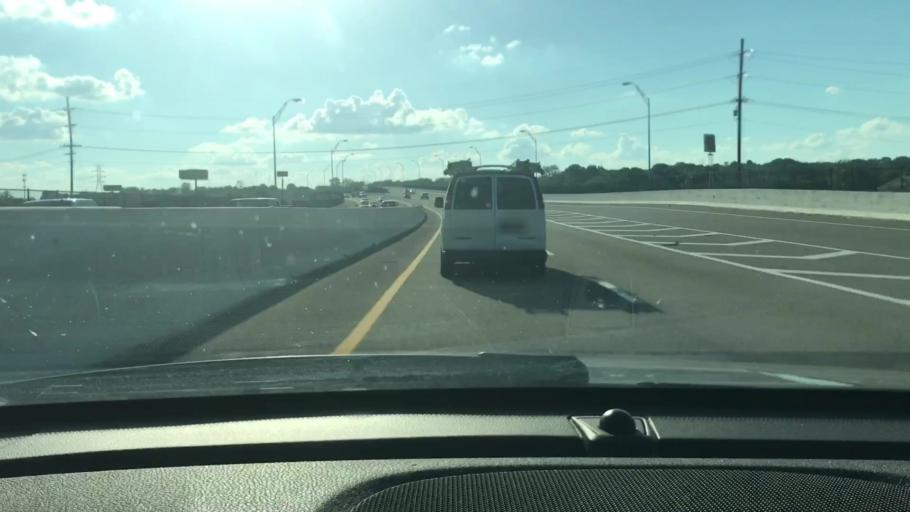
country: US
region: Tennessee
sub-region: Davidson County
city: Goodlettsville
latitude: 36.3060
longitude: -86.7019
